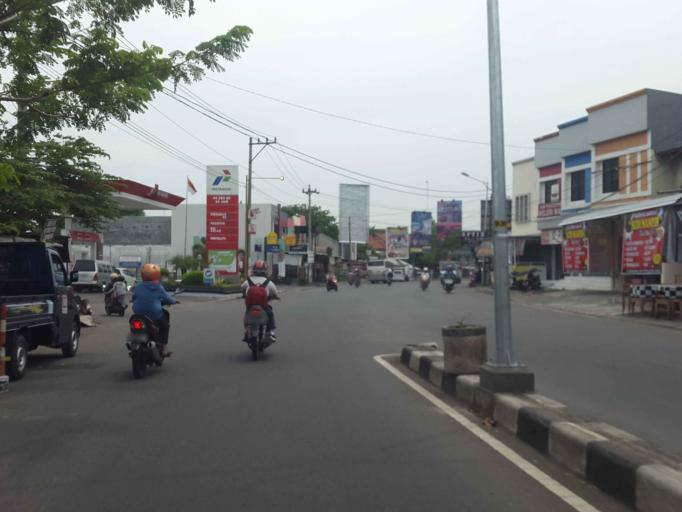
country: ID
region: Central Java
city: Semarang
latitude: -7.0238
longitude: 110.4593
